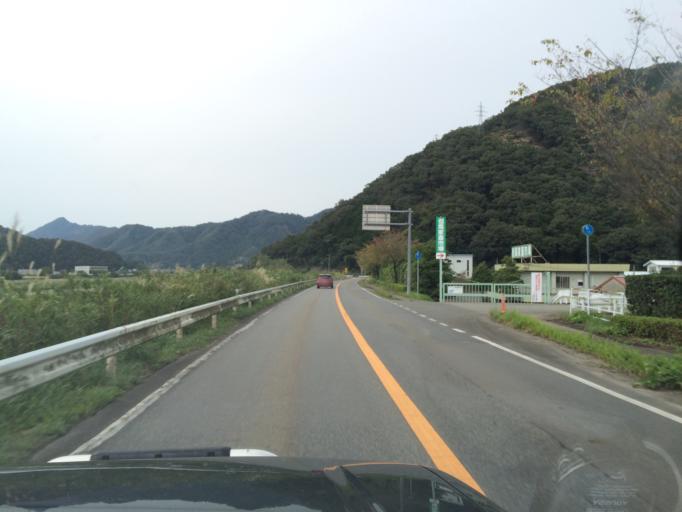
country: JP
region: Hyogo
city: Toyooka
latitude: 35.3939
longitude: 134.7933
